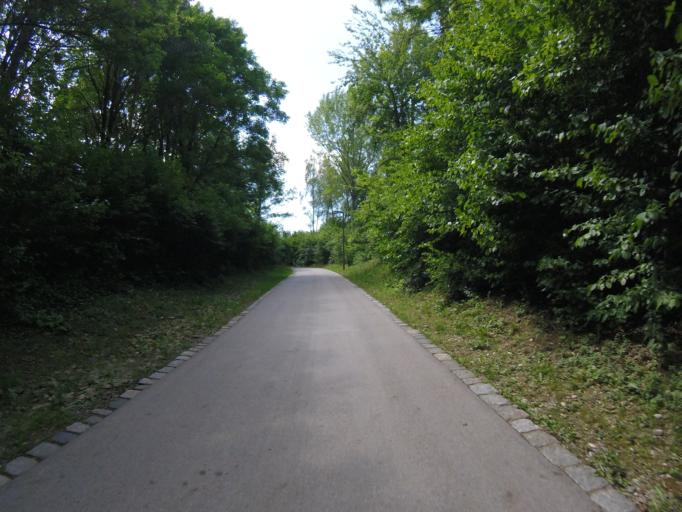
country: DE
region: Bavaria
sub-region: Upper Bavaria
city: Unterhaching
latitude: 48.0735
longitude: 11.6114
